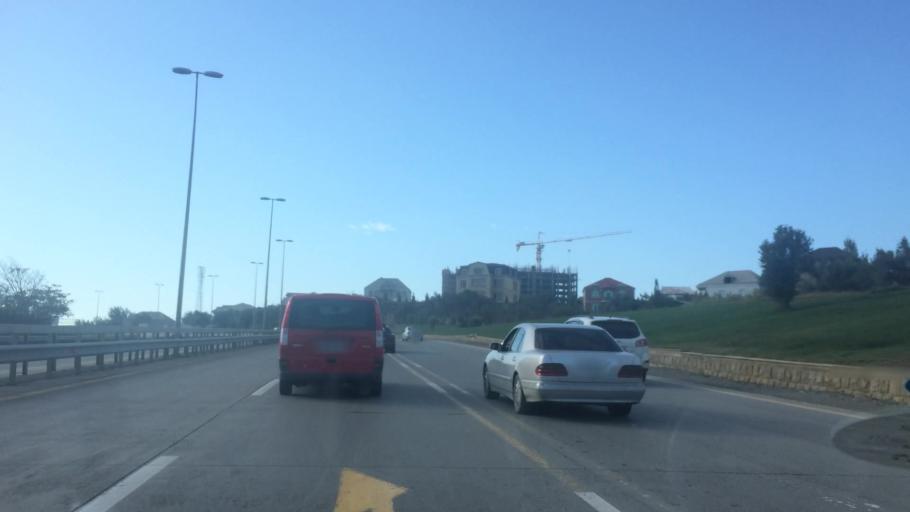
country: AZ
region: Baki
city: Qaracuxur
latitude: 40.3482
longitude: 49.9664
